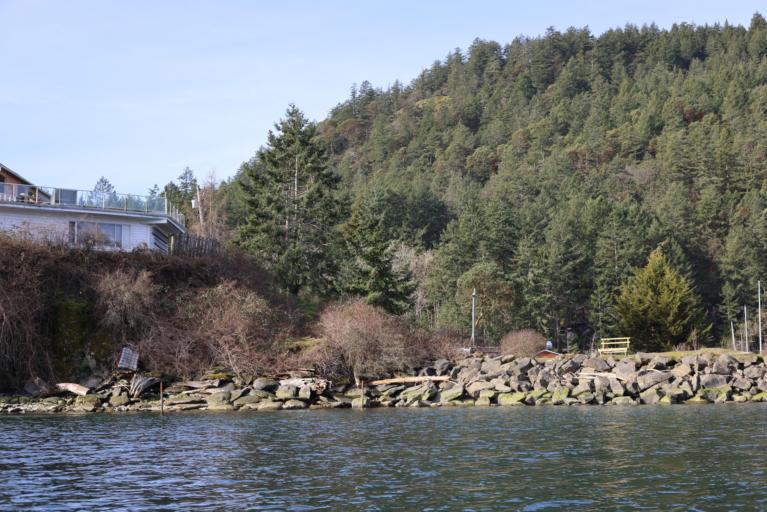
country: CA
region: British Columbia
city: Duncan
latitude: 48.7589
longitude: -123.5965
